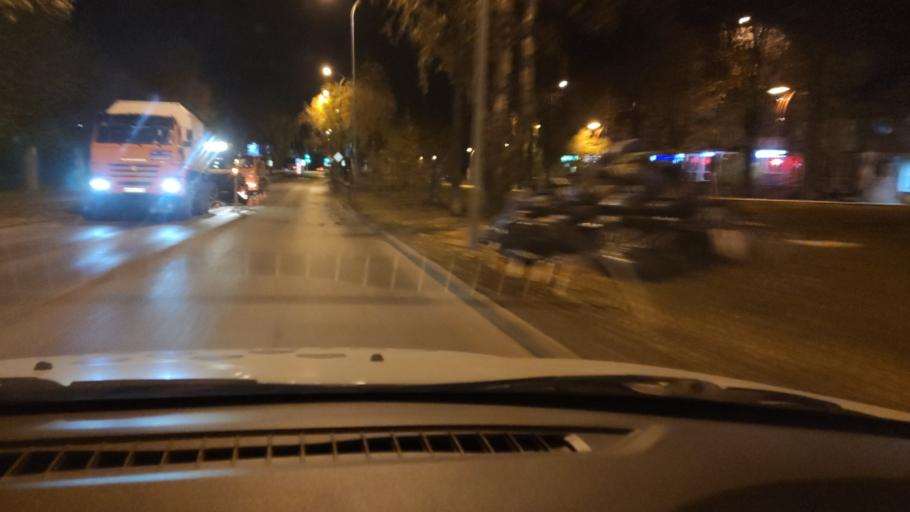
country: RU
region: Perm
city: Perm
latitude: 57.9807
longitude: 56.1817
